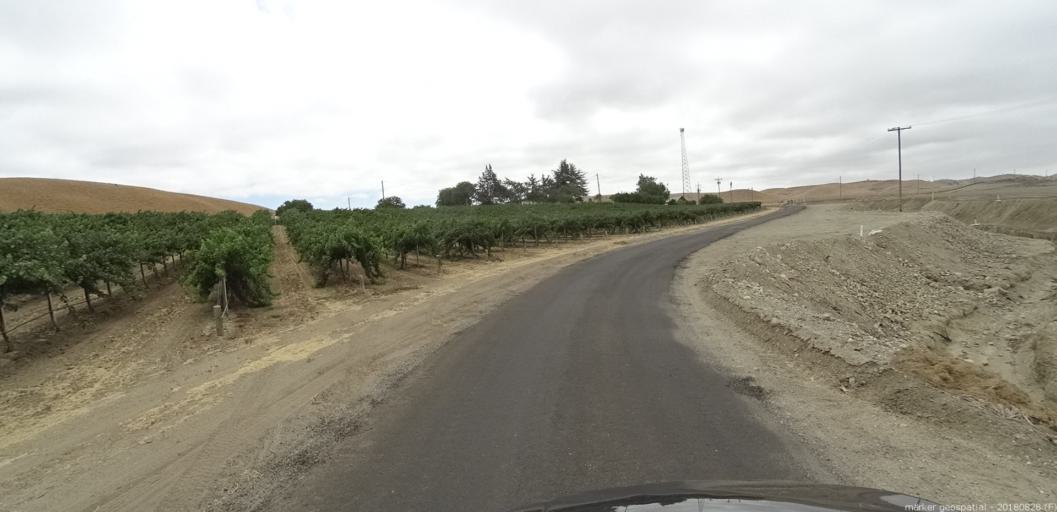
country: US
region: California
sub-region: San Luis Obispo County
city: Lake Nacimiento
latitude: 35.9784
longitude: -120.8701
